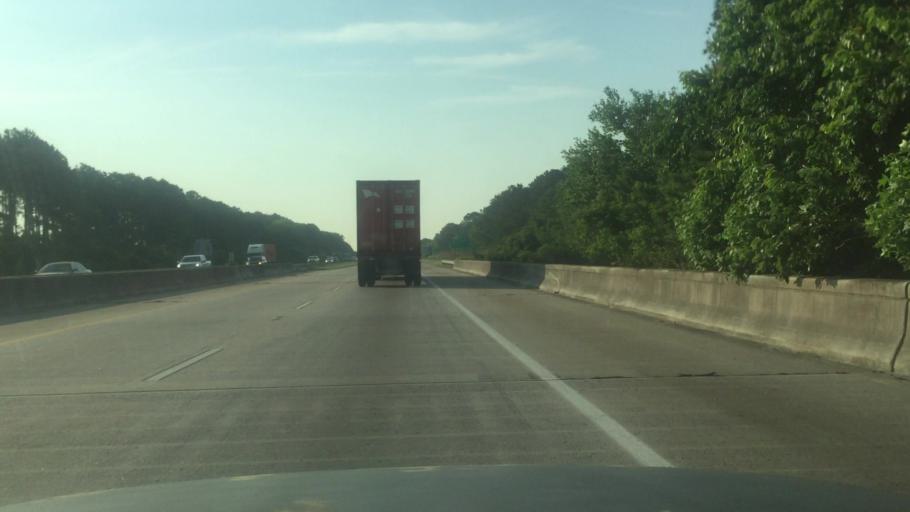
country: US
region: South Carolina
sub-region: Charleston County
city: Mount Pleasant
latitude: 32.8507
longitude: -79.8823
